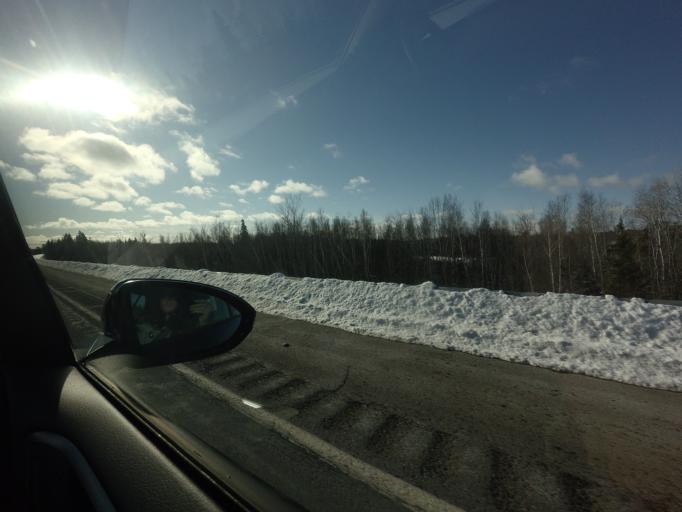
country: CA
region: New Brunswick
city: Fredericton
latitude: 45.8967
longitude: -66.6496
